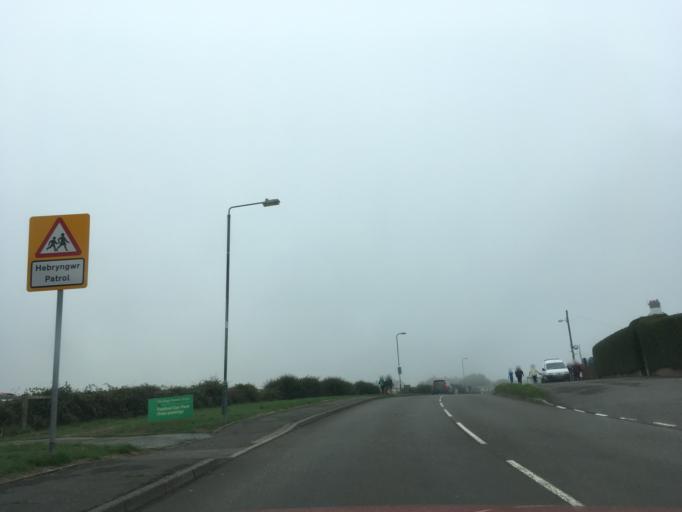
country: GB
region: Wales
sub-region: Pembrokeshire
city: Saint David's
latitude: 51.8743
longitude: -5.2000
